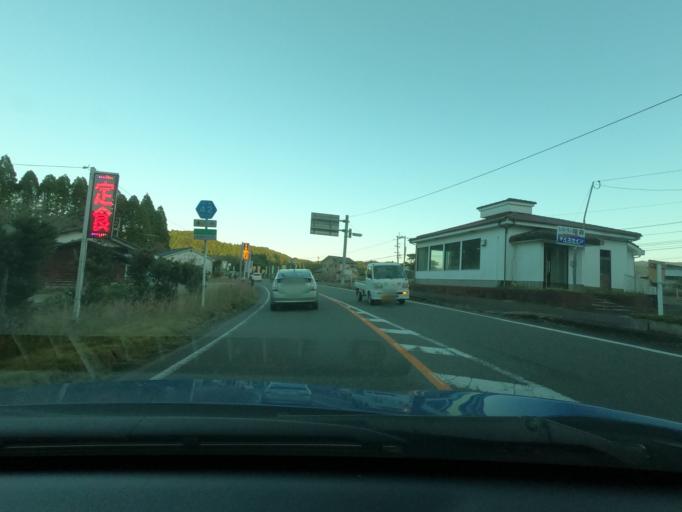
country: JP
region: Kagoshima
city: Satsumasendai
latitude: 31.7963
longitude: 130.4051
